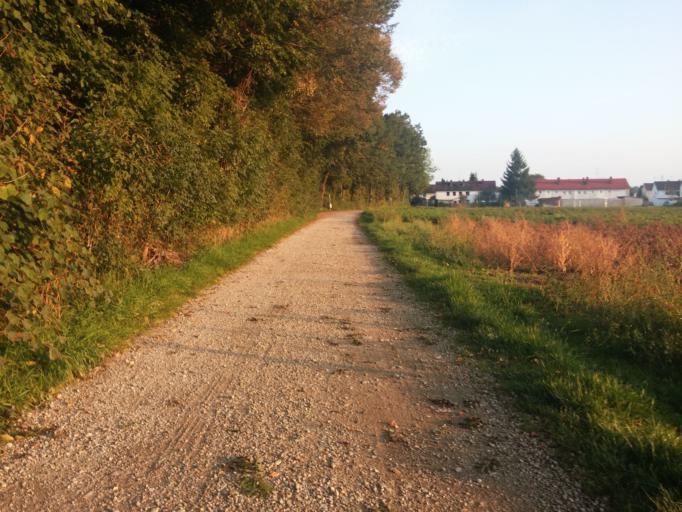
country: DE
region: Bavaria
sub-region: Upper Bavaria
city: Zorneding
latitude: 48.0971
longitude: 11.8403
